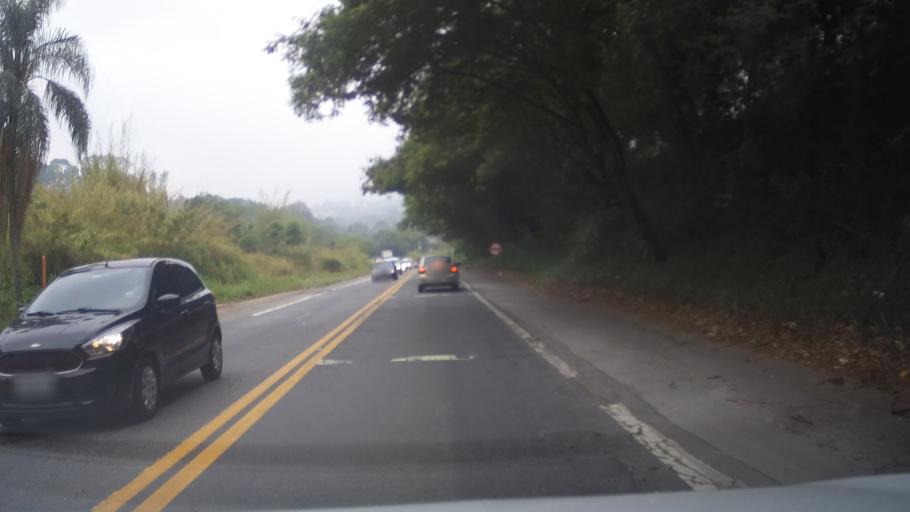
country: BR
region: Sao Paulo
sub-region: Itatiba
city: Itatiba
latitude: -23.0013
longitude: -46.8112
